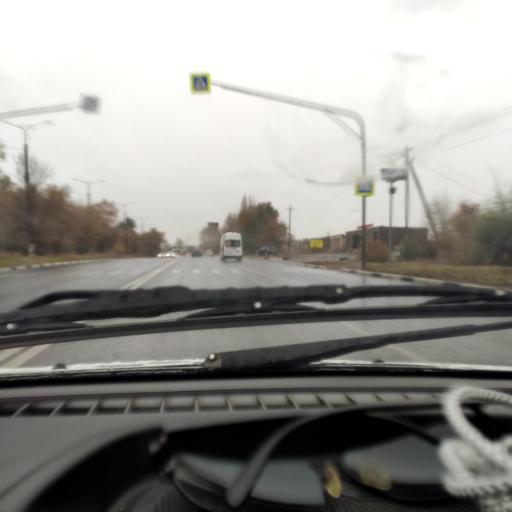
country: RU
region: Samara
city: Zhigulevsk
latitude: 53.4900
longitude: 49.4742
